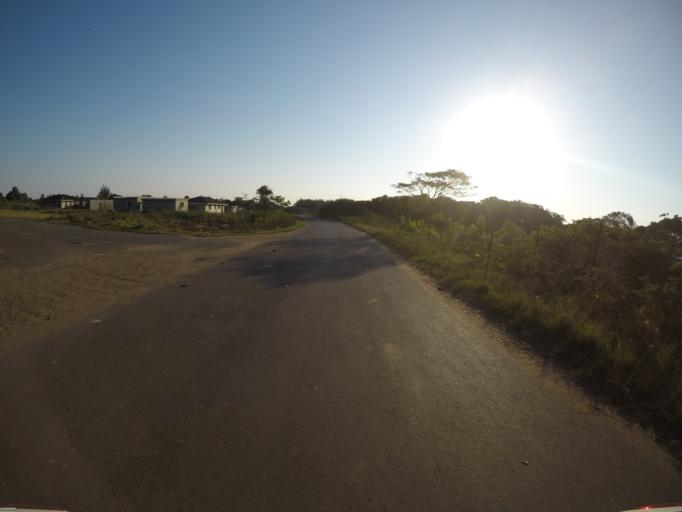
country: ZA
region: KwaZulu-Natal
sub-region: uThungulu District Municipality
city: KwaMbonambi
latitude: -28.7072
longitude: 32.1802
